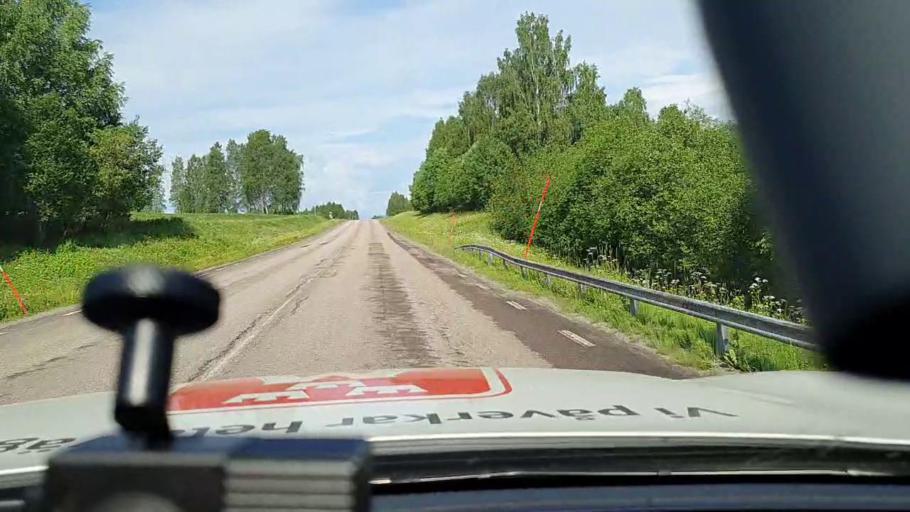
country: SE
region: Norrbotten
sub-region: Alvsbyns Kommun
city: AElvsbyn
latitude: 66.0140
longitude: 21.1664
